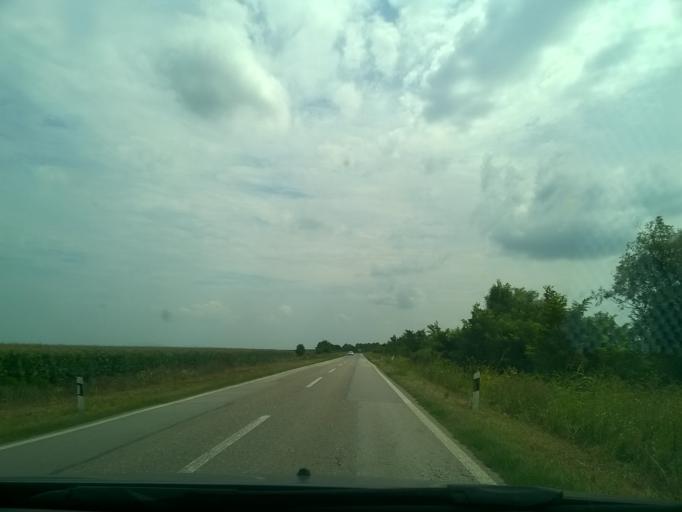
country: RS
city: Hajducica
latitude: 45.2346
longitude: 20.9934
